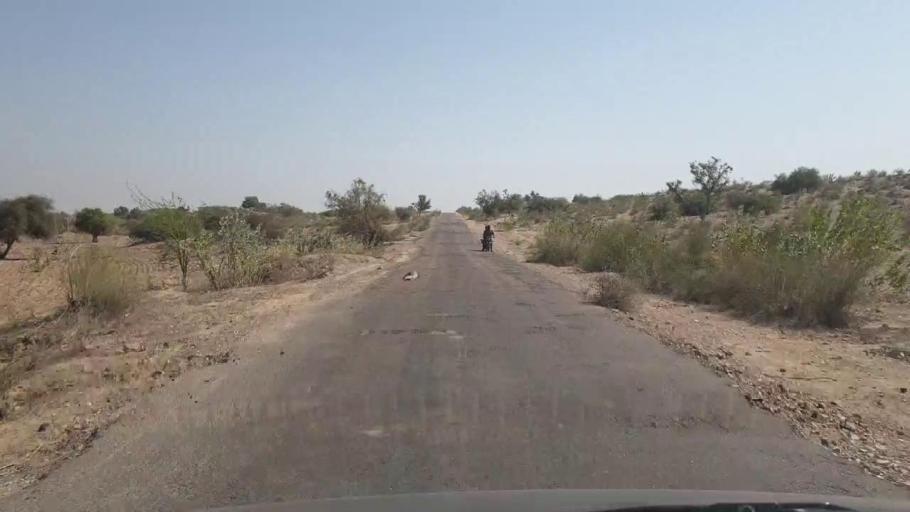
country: PK
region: Sindh
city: Chor
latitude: 25.5998
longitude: 69.9812
